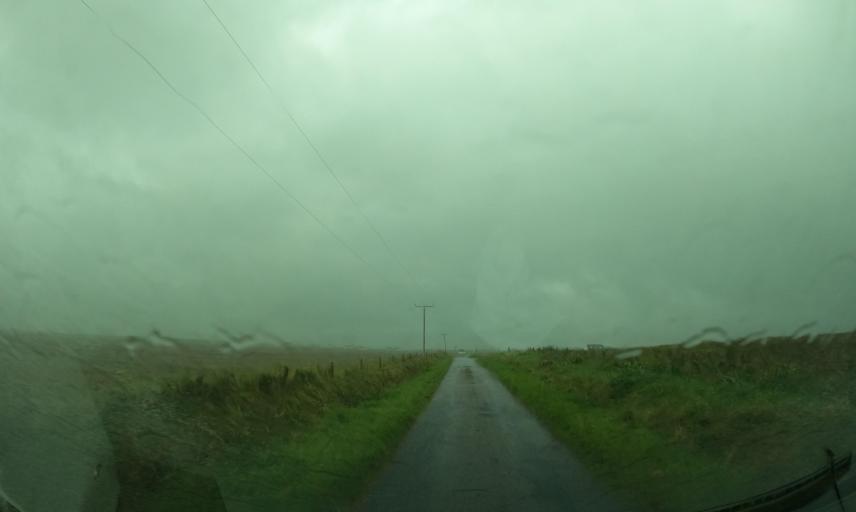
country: GB
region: Scotland
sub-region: Eilean Siar
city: Barra
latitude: 56.4680
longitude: -6.9122
